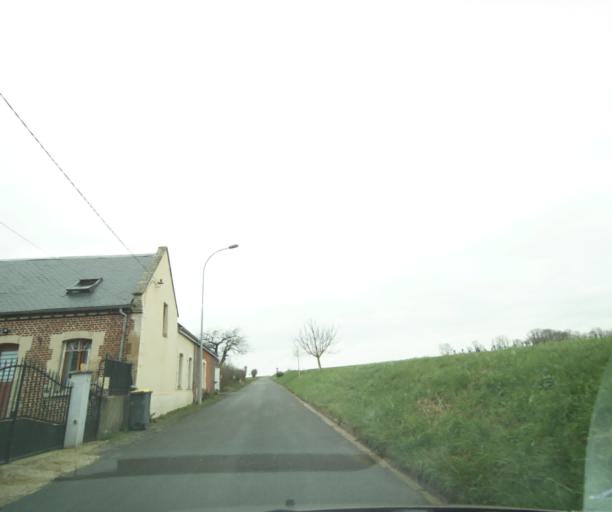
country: FR
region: Picardie
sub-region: Departement de l'Oise
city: Noyon
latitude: 49.5995
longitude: 3.0144
